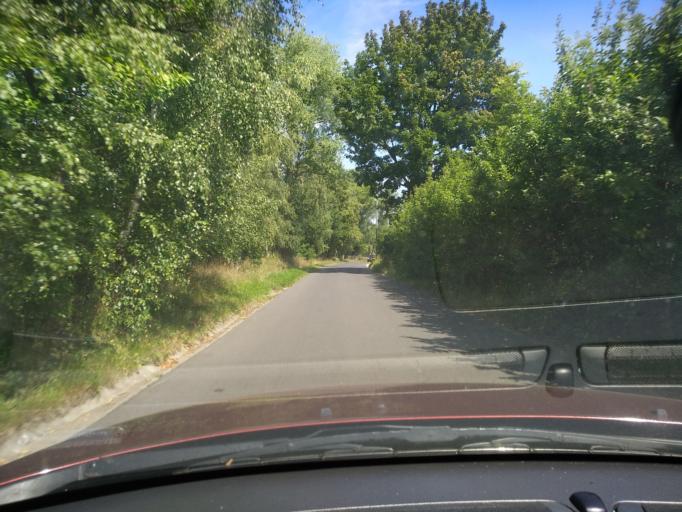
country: PL
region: Lower Silesian Voivodeship
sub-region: Powiat lwowecki
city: Mirsk
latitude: 50.9697
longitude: 15.3381
